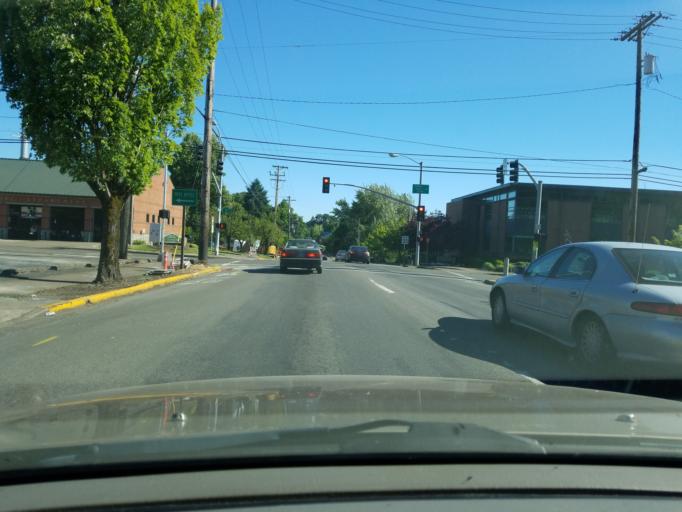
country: US
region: Oregon
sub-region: Yamhill County
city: McMinnville
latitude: 45.2096
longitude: -123.1991
